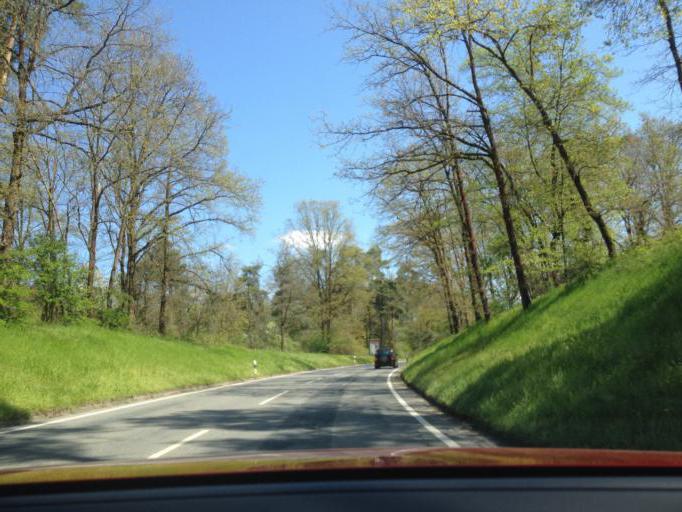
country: DE
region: Bavaria
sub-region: Regierungsbezirk Mittelfranken
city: Neunkirchen am Sand
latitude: 49.5198
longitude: 11.3098
